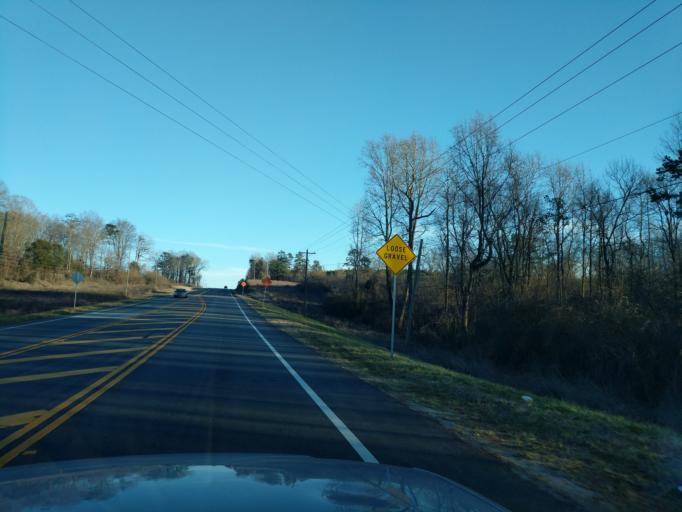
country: US
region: Georgia
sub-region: Stephens County
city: Toccoa
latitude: 34.5190
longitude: -83.2370
